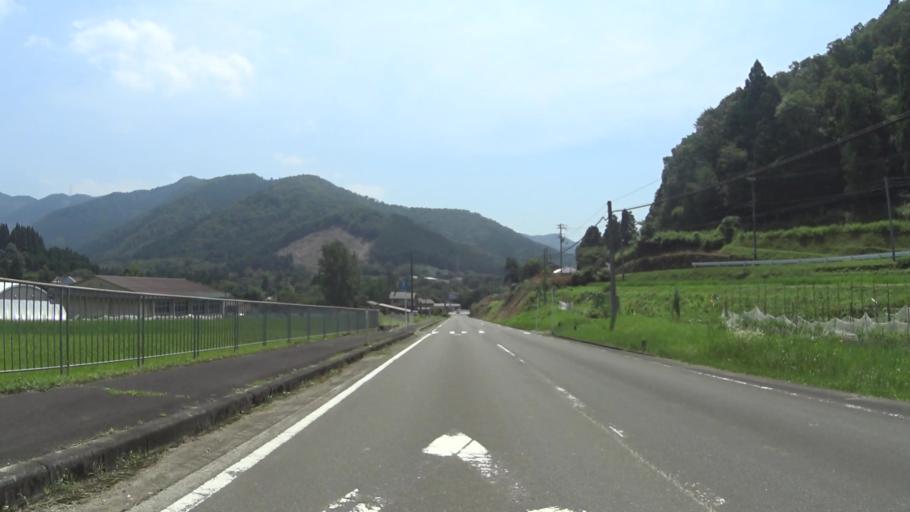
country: JP
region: Kyoto
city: Ayabe
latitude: 35.2675
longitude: 135.4305
